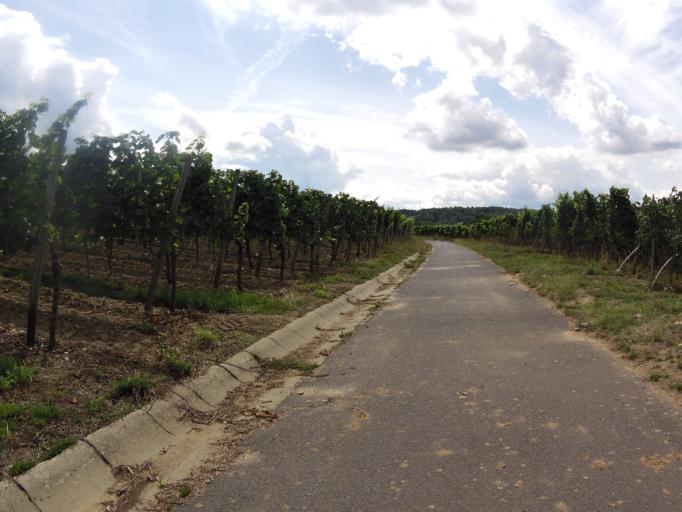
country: DE
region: Bavaria
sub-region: Regierungsbezirk Unterfranken
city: Sommerhausen
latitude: 49.6888
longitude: 10.0291
